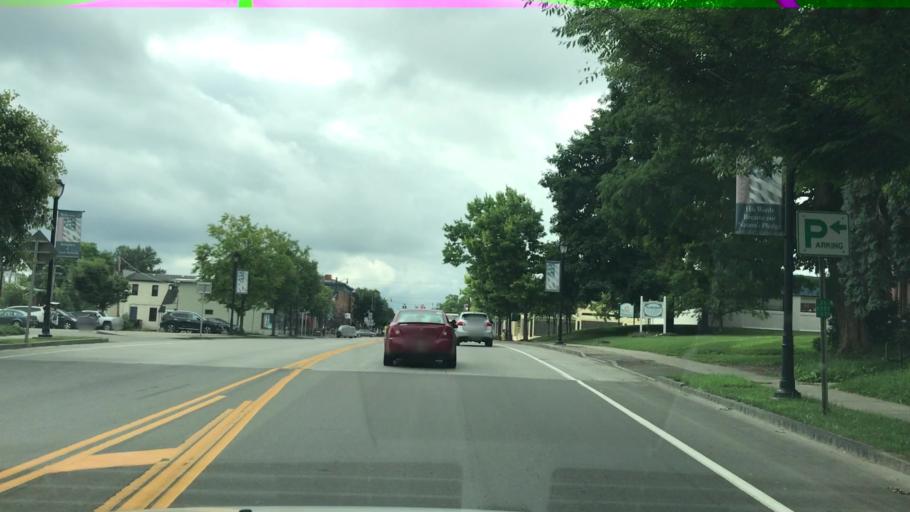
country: US
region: New York
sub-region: Livingston County
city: Mount Morris
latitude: 42.7273
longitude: -77.8751
